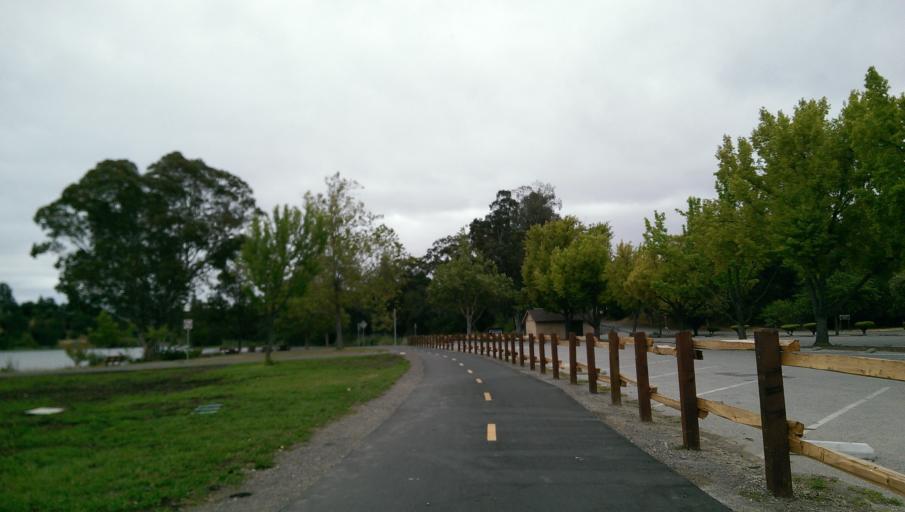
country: US
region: California
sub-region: Santa Clara County
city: Los Gatos
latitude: 37.2405
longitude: -121.9686
